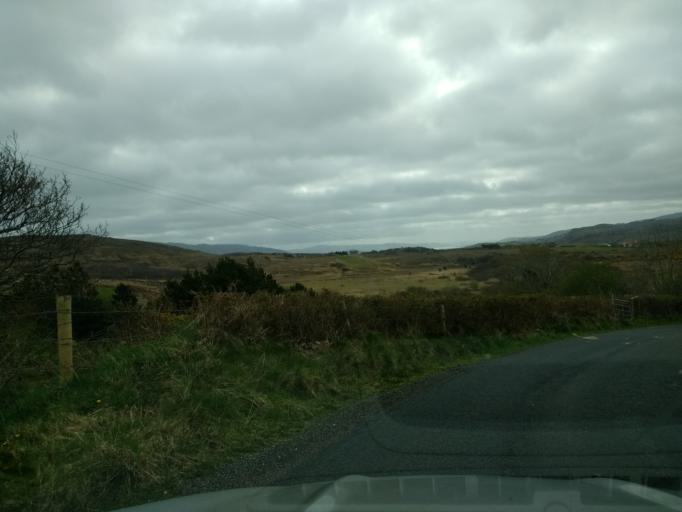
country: IE
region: Ulster
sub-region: County Donegal
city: Ramelton
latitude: 55.2616
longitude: -7.6363
